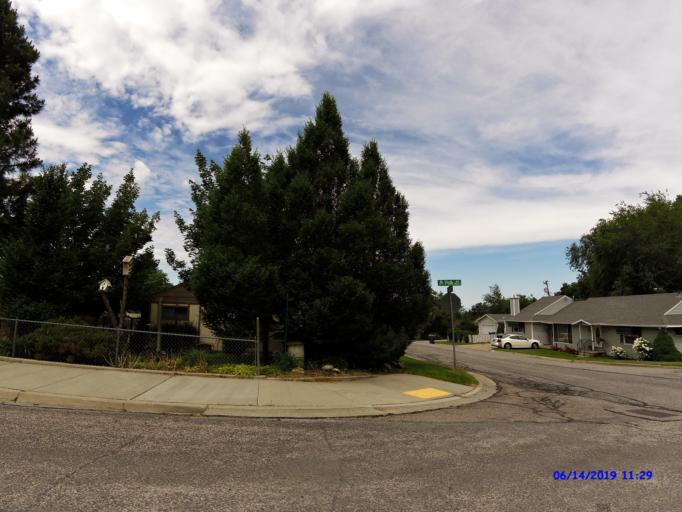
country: US
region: Utah
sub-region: Weber County
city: Ogden
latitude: 41.2554
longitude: -111.9425
